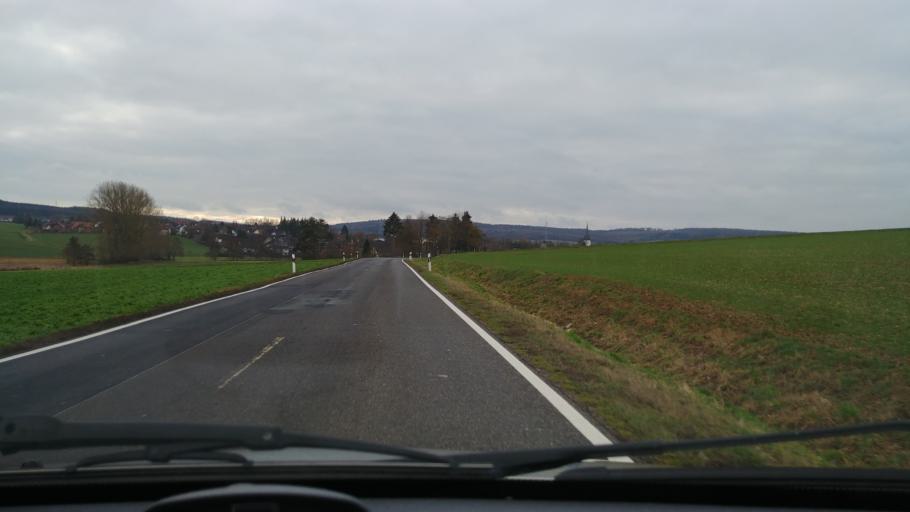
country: DE
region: Rheinland-Pfalz
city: Netzbach
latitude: 50.3187
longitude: 8.1641
